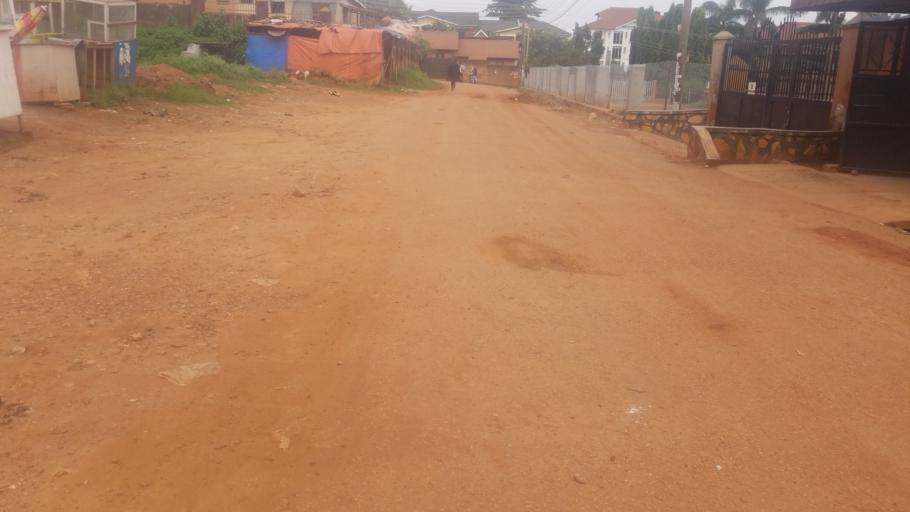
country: UG
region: Central Region
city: Kampala Central Division
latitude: 0.3323
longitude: 32.5622
